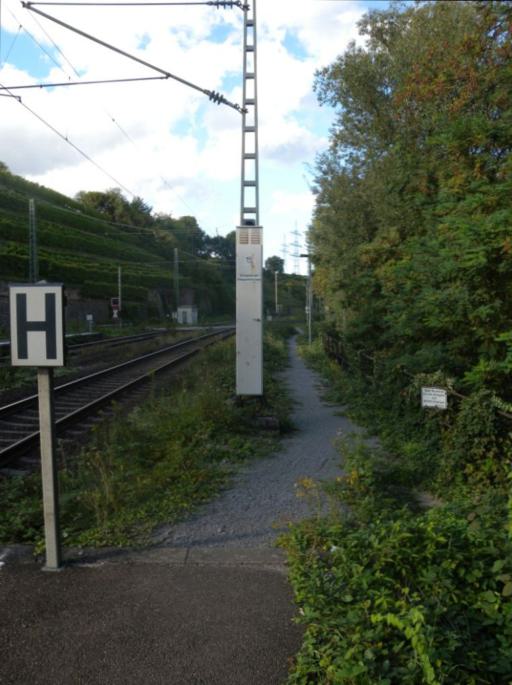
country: DE
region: Baden-Wuerttemberg
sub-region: Regierungsbezirk Stuttgart
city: Nordheim
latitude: 49.1097
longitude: 9.1491
